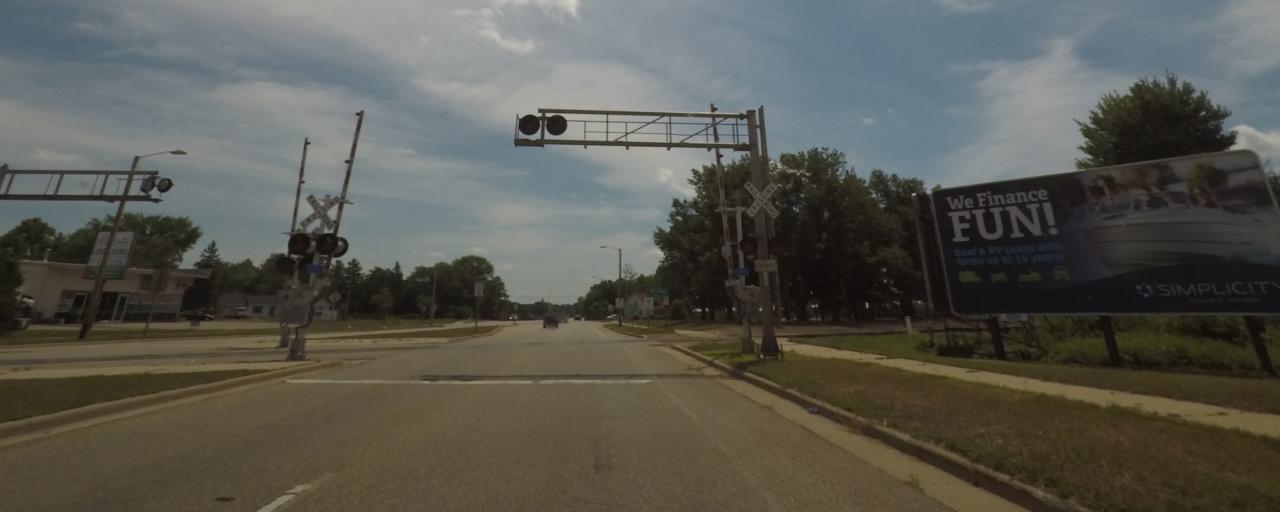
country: US
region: Wisconsin
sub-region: Portage County
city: Whiting
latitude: 44.4975
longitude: -89.5605
